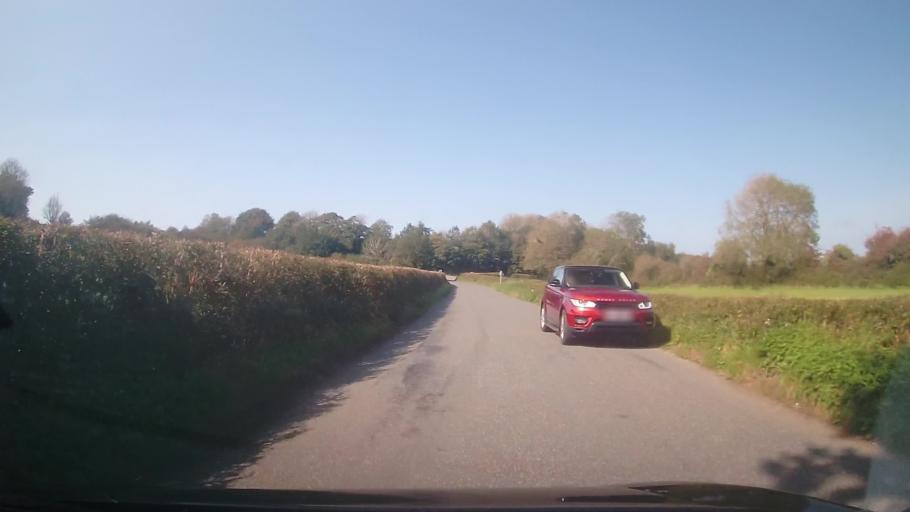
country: GB
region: Wales
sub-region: Pembrokeshire
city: Camrose
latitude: 51.8399
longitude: -4.9854
